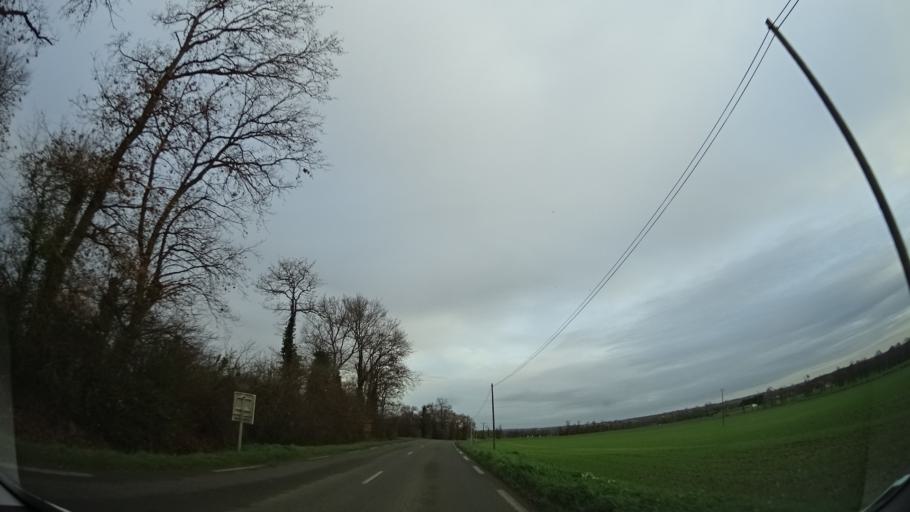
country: FR
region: Brittany
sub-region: Departement des Cotes-d'Armor
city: Evran
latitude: 48.3651
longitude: -1.9705
